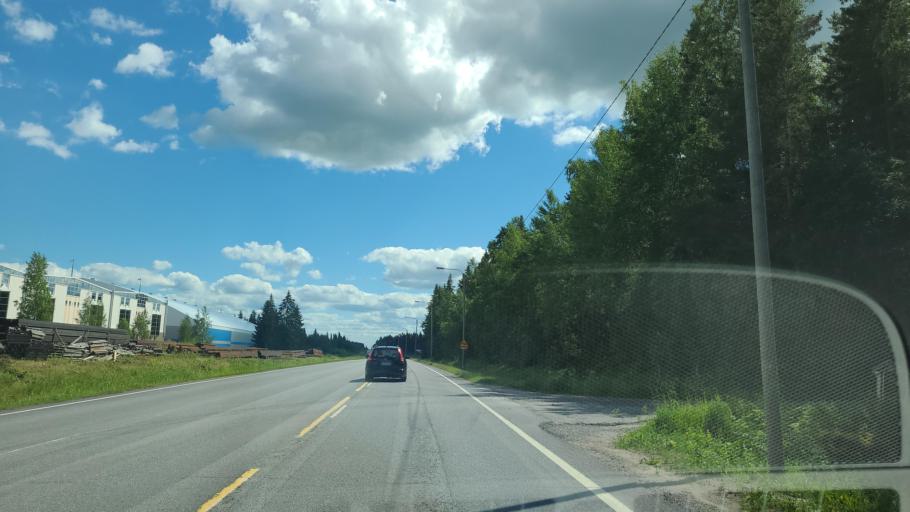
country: FI
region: Southern Ostrobothnia
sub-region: Seinaejoki
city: Ylistaro
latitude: 62.8875
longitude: 22.6541
